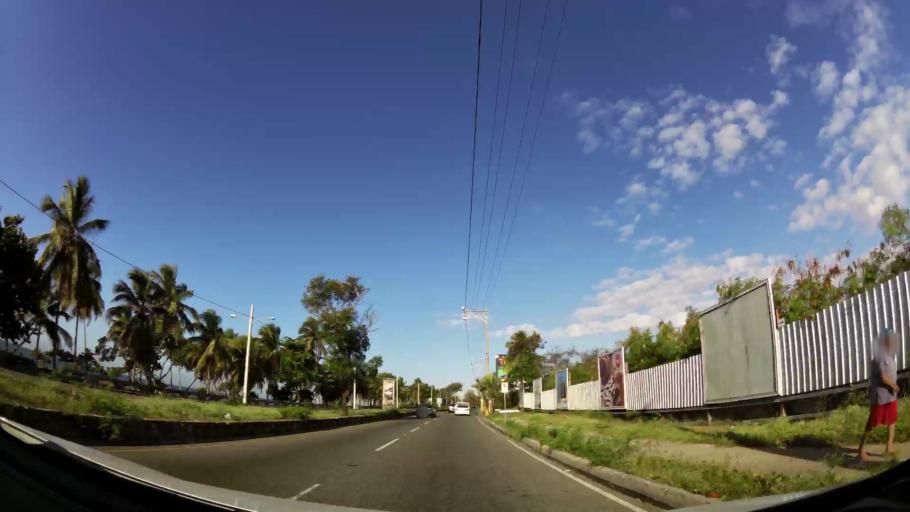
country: DO
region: Santo Domingo
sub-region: Santo Domingo
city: Santo Domingo Este
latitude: 18.4684
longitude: -69.8382
